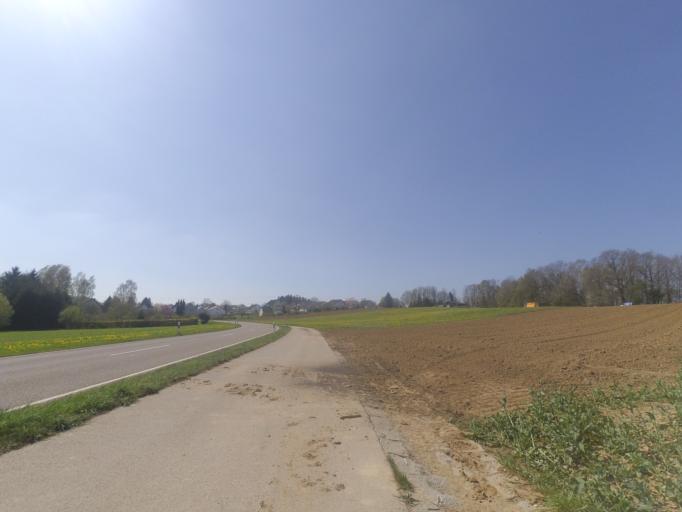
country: DE
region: Bavaria
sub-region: Swabia
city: Roggenburg
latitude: 48.3166
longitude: 10.2104
